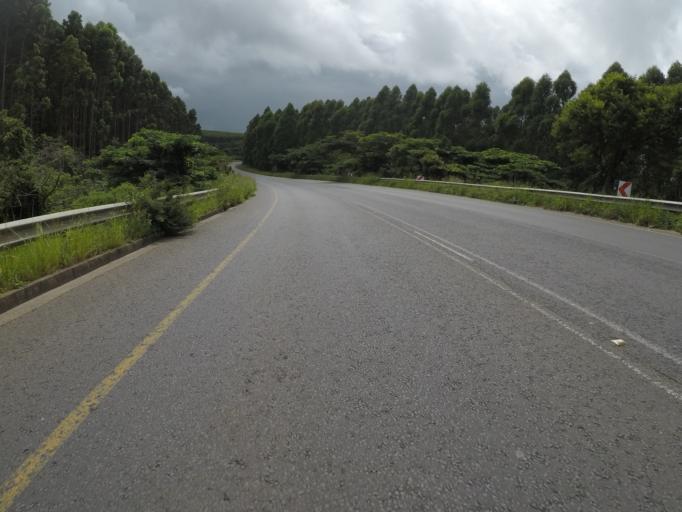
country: ZA
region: KwaZulu-Natal
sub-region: uThungulu District Municipality
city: eSikhawini
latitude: -28.8654
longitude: 31.8894
